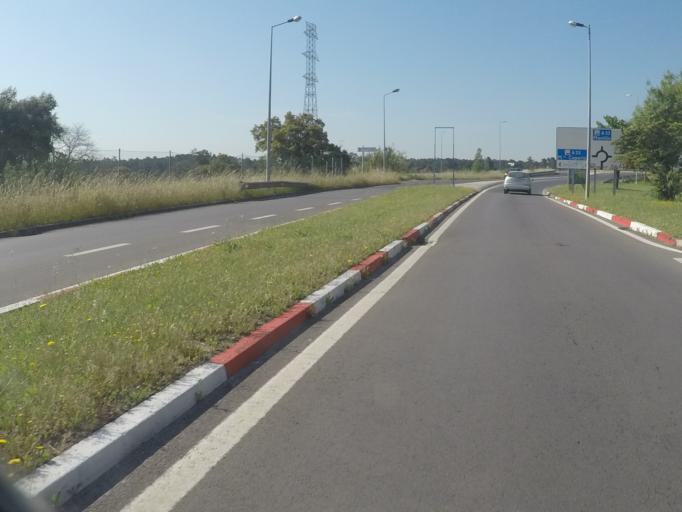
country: PT
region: Setubal
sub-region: Seixal
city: Amora
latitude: 38.6049
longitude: -9.1292
